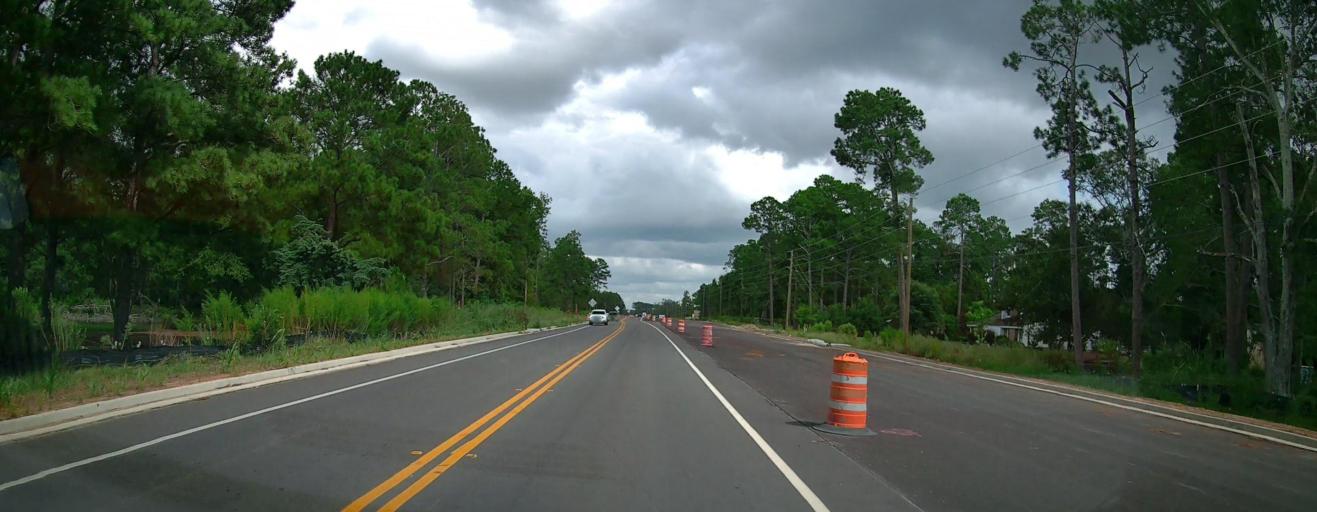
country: US
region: Georgia
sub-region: Coffee County
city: Douglas
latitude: 31.5260
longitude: -82.9032
